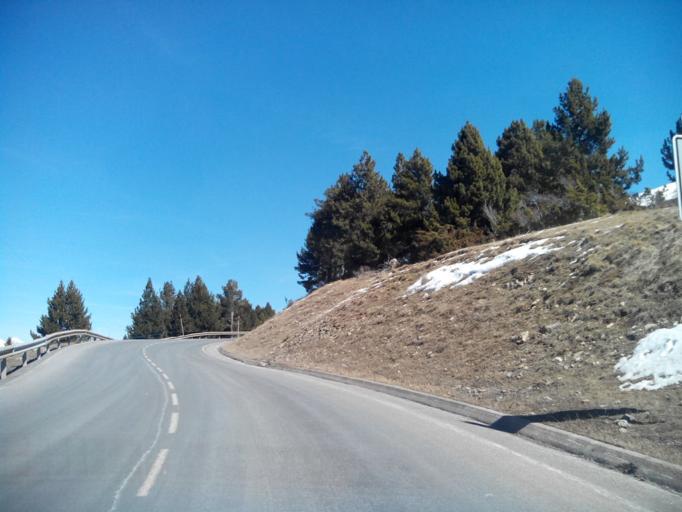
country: ES
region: Catalonia
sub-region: Provincia de Girona
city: Toses
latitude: 42.3253
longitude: 1.9579
